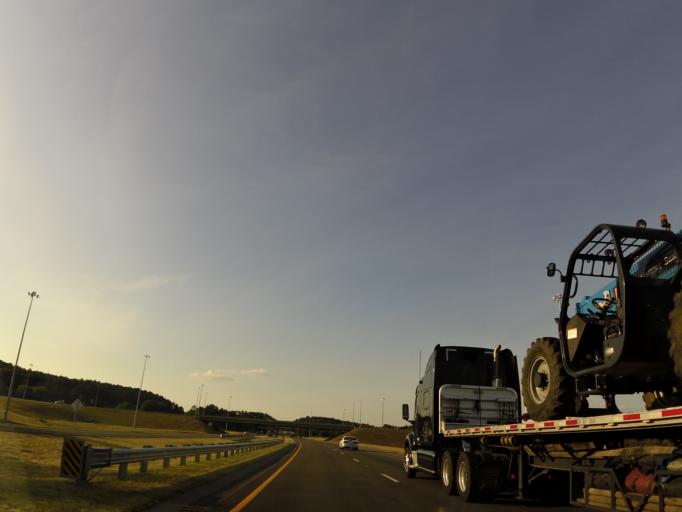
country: US
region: Alabama
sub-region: DeKalb County
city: Fort Payne
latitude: 34.5024
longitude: -85.6933
